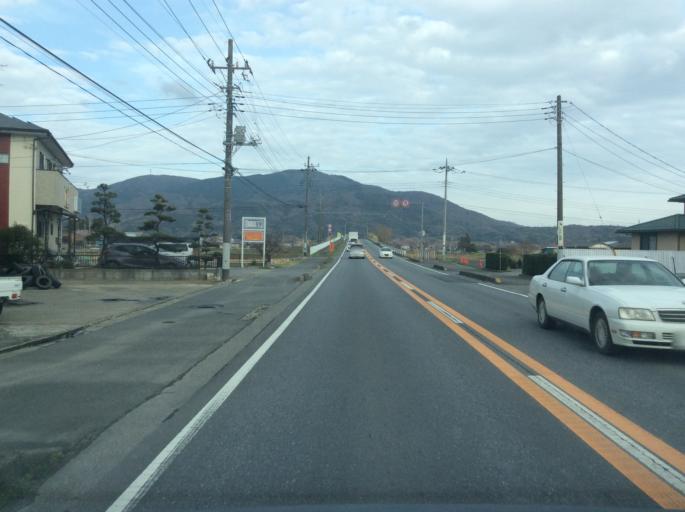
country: JP
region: Ibaraki
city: Tsukuba
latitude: 36.1731
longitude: 140.0913
